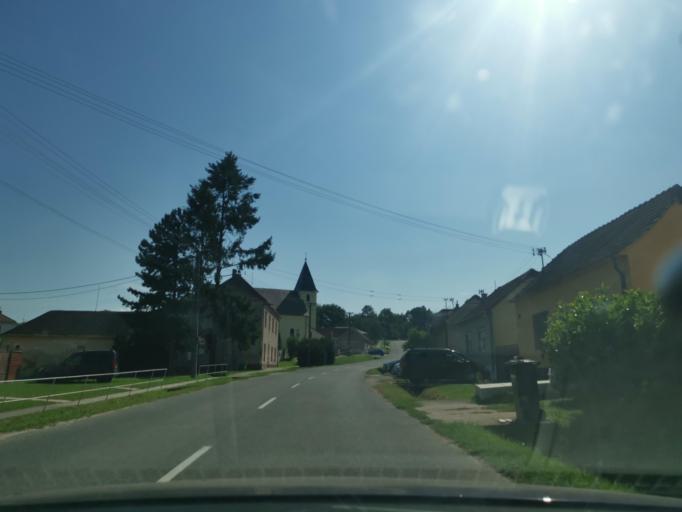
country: SK
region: Trnavsky
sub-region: Okres Senica
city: Senica
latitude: 48.7020
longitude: 17.2808
